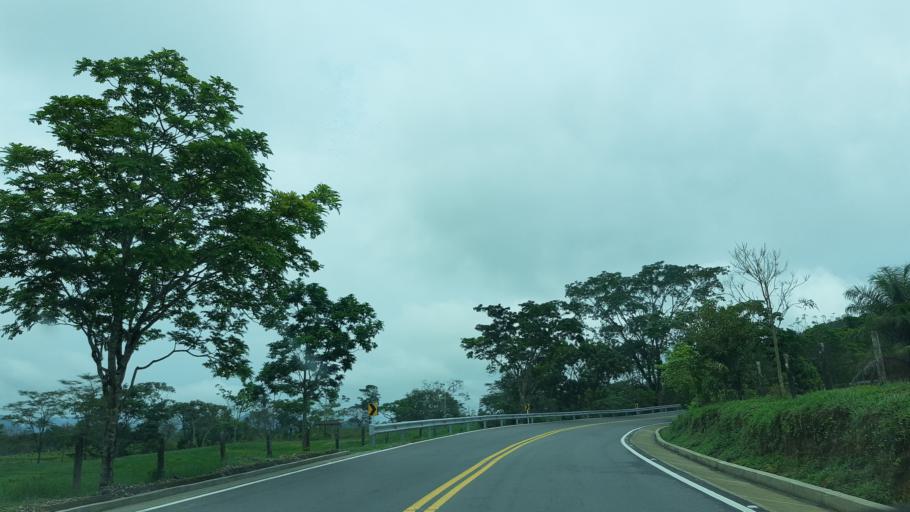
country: CO
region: Casanare
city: Sabanalarga
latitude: 4.7714
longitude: -73.0398
